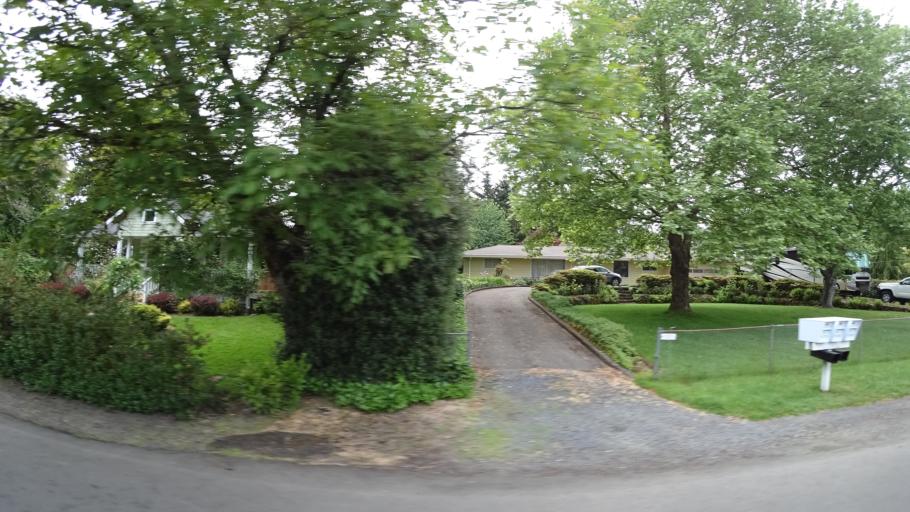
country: US
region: Oregon
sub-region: Washington County
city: Garden Home-Whitford
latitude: 45.4680
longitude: -122.7471
